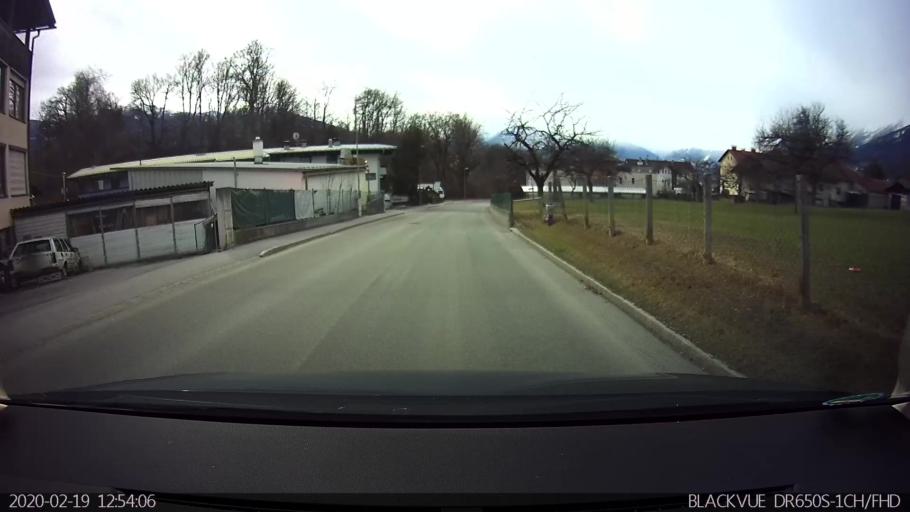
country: AT
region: Tyrol
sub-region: Politischer Bezirk Innsbruck Land
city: Absam
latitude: 47.3011
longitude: 11.5131
